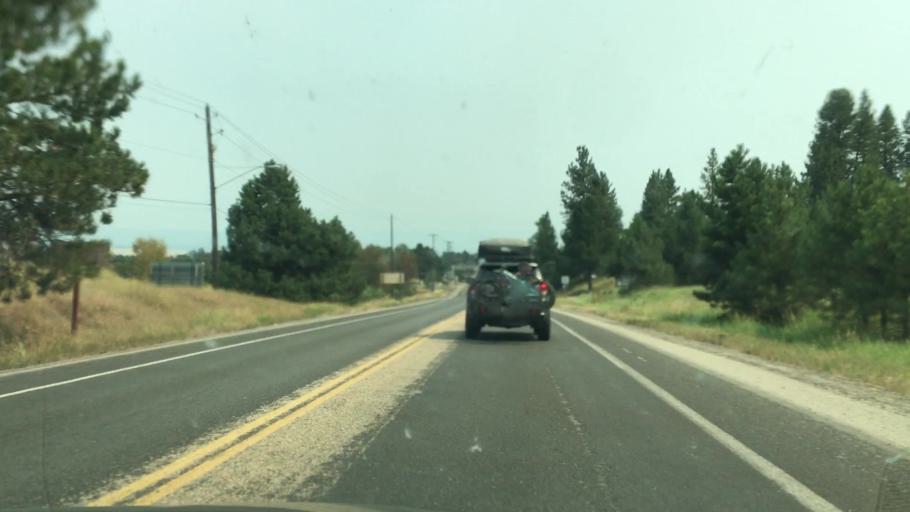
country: US
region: Idaho
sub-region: Valley County
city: Cascade
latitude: 44.5086
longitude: -116.0342
